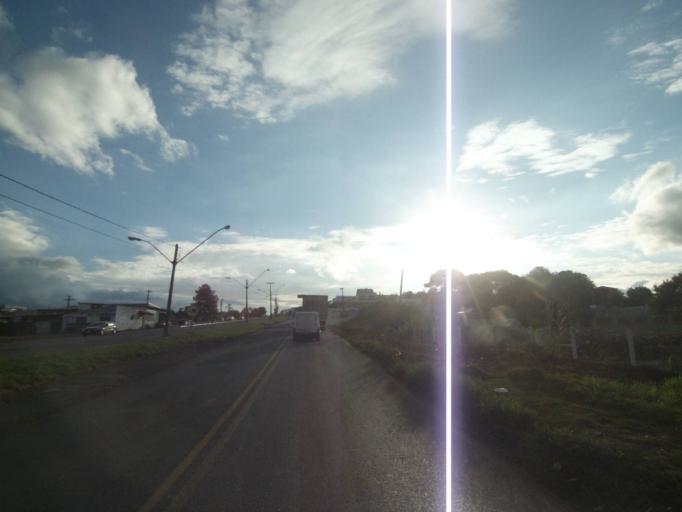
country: BR
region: Parana
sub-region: Telemaco Borba
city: Telemaco Borba
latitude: -24.3270
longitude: -50.6331
